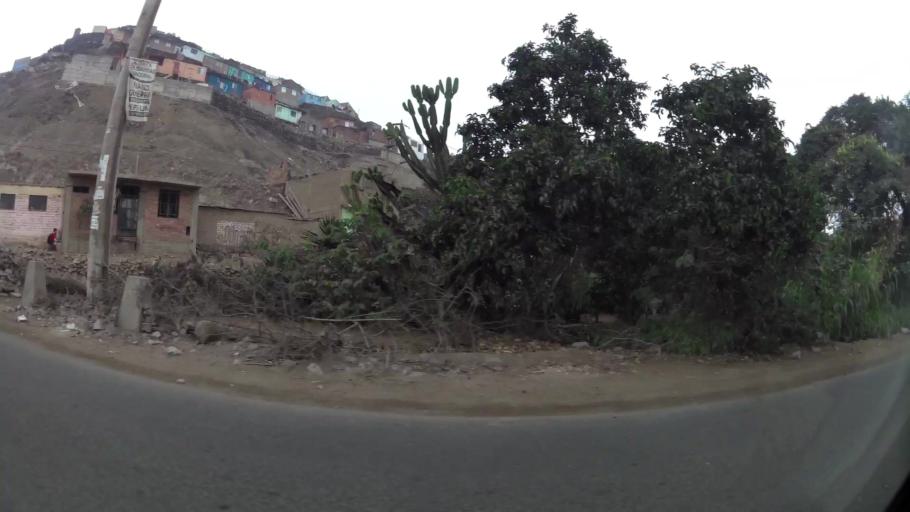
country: PE
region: Lima
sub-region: Lima
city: Urb. Santo Domingo
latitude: -11.8751
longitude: -77.0743
